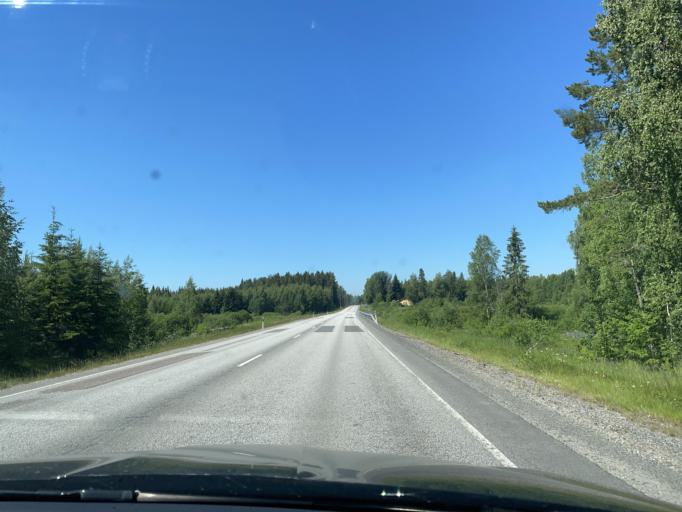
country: FI
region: Central Finland
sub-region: Saarijaervi-Viitasaari
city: Viitasaari
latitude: 63.1434
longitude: 25.8215
